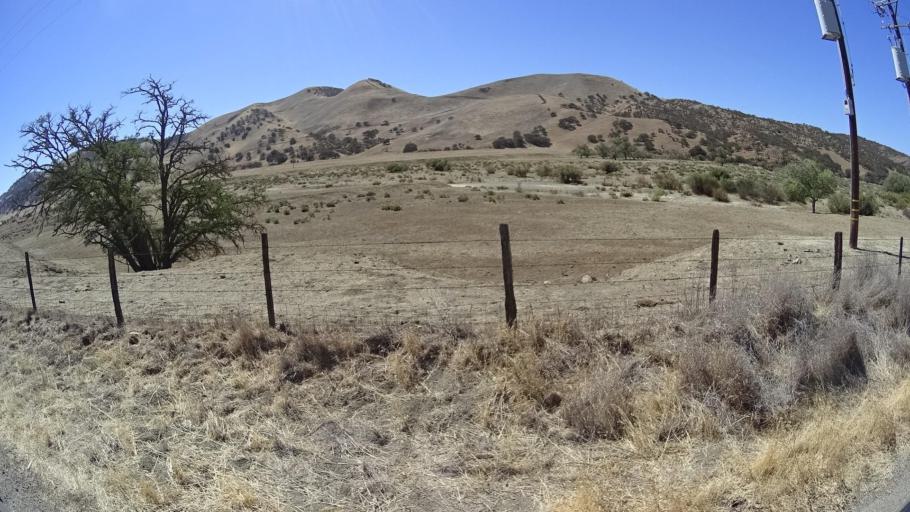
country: US
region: California
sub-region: Monterey County
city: King City
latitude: 36.2818
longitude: -120.9577
